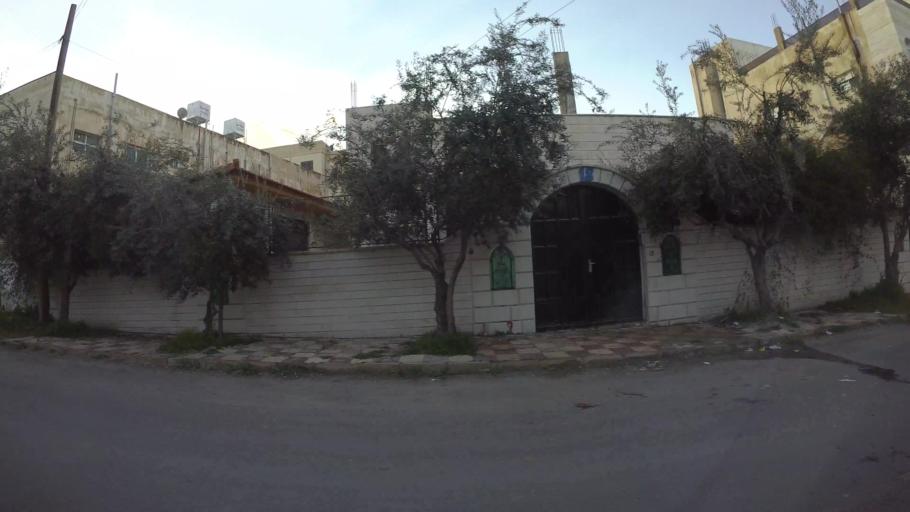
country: JO
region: Amman
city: Al Bunayyat ash Shamaliyah
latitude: 31.9052
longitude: 35.9060
